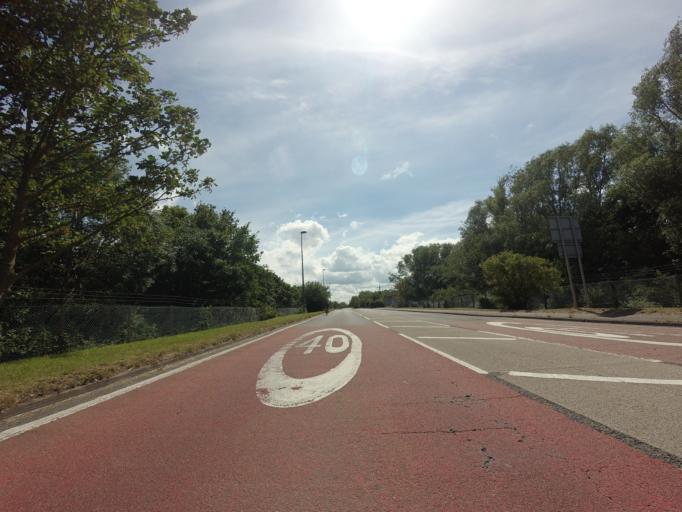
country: GB
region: England
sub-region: Medway
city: Allhallows
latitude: 51.4458
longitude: 0.6925
